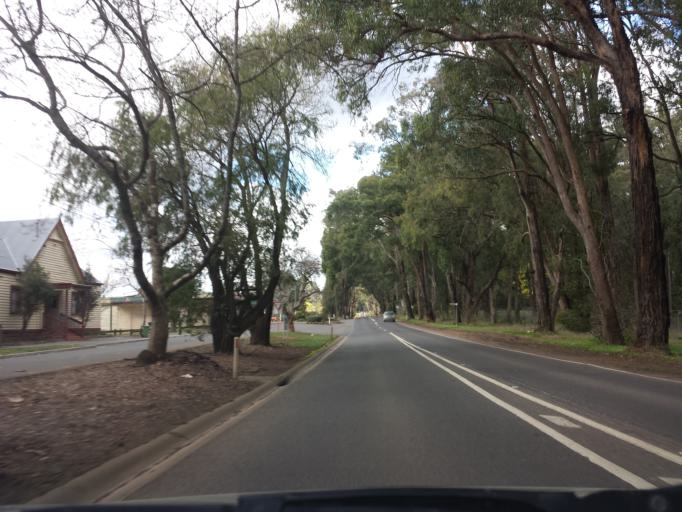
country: AU
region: Victoria
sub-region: Yarra Ranges
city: Kalorama
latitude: -37.8247
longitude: 145.4210
